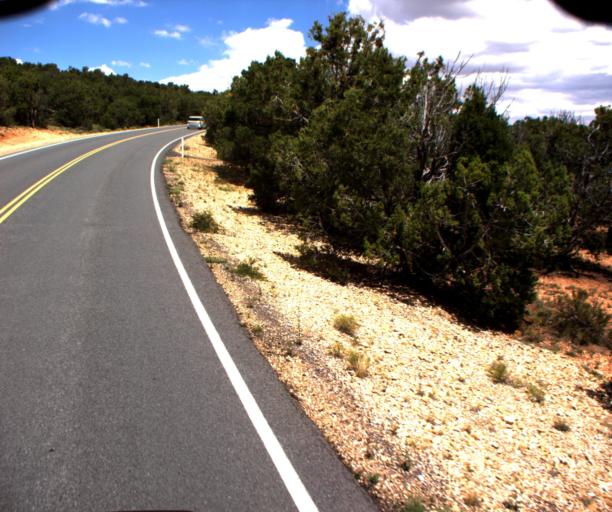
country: US
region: Arizona
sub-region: Coconino County
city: Grand Canyon
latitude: 36.0117
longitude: -111.8084
